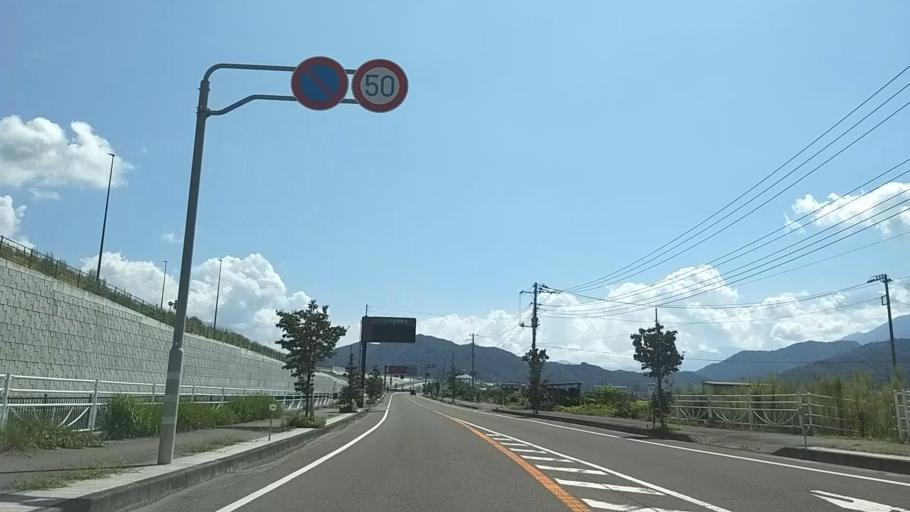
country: JP
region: Yamanashi
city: Ryuo
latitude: 35.5642
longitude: 138.4726
